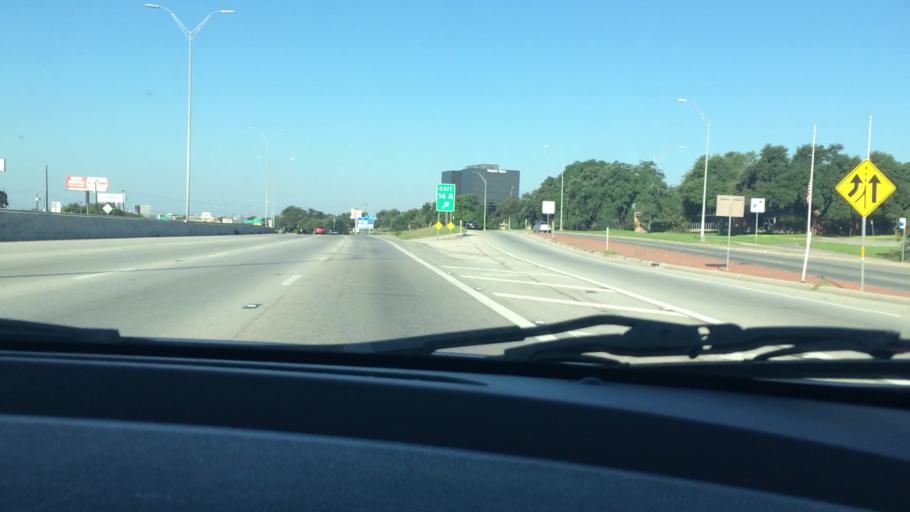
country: US
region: Texas
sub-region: Bexar County
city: Balcones Heights
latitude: 29.4897
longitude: -98.5754
